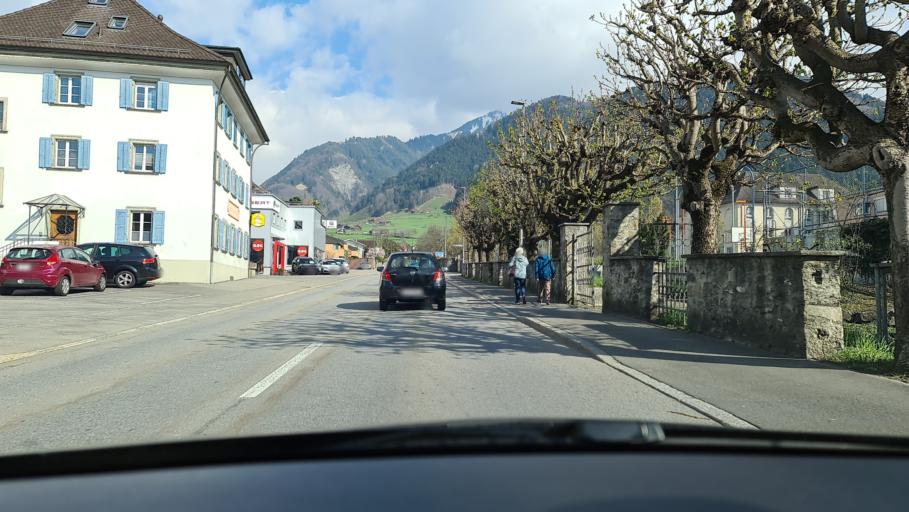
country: CH
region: Uri
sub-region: Uri
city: Altdorf
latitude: 46.8752
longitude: 8.6507
